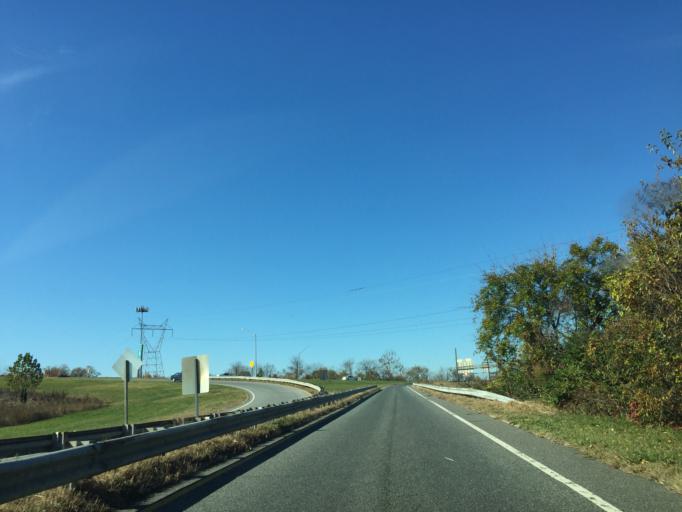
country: US
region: Maryland
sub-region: Anne Arundel County
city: Linthicum
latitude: 39.2207
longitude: -76.6574
